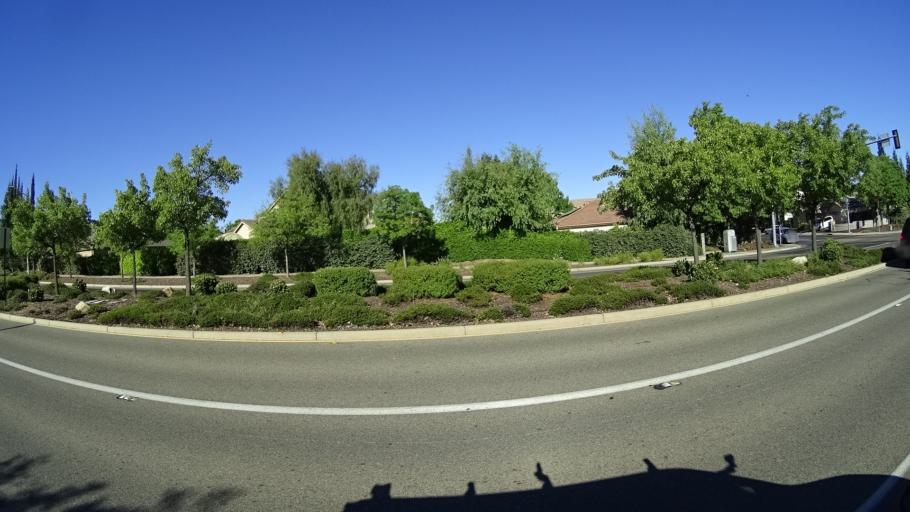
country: US
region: California
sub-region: Placer County
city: Rocklin
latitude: 38.7971
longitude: -121.2764
